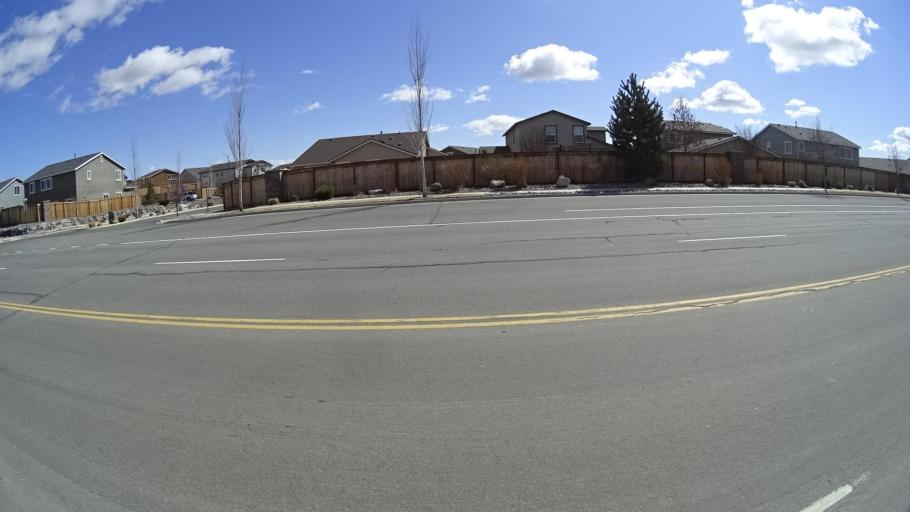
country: US
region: Nevada
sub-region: Washoe County
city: Lemmon Valley
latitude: 39.6493
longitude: -119.8762
